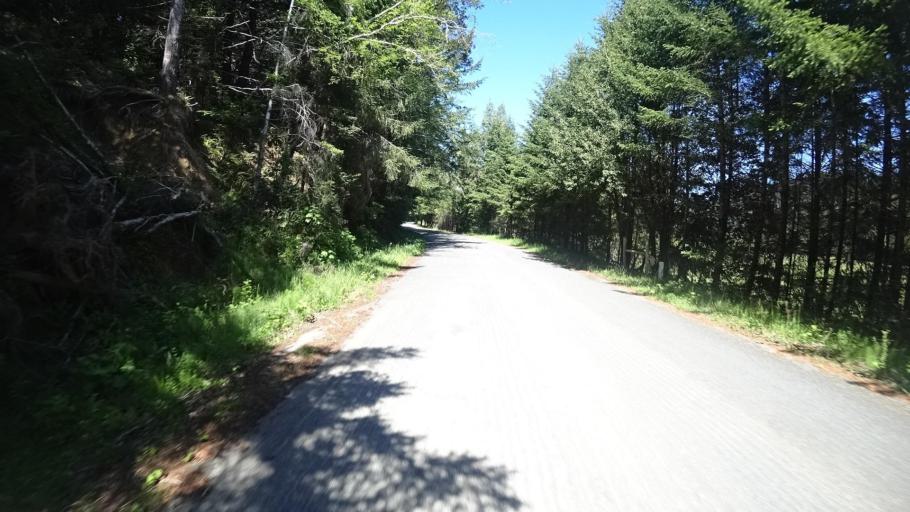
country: US
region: California
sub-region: Humboldt County
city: Rio Dell
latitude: 40.2669
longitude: -124.1988
